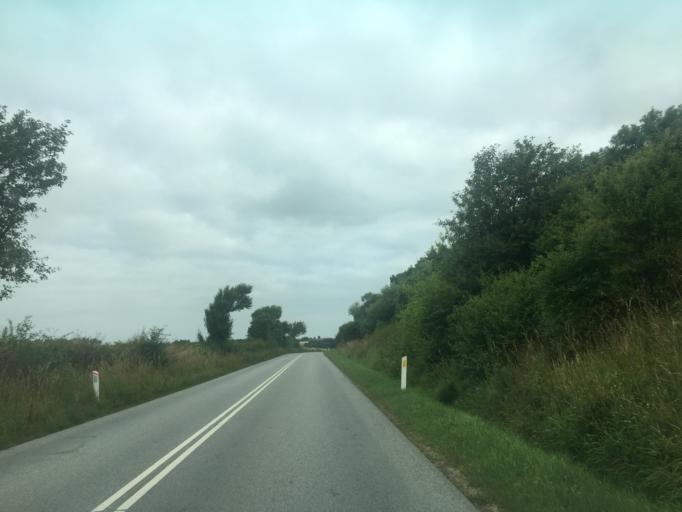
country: DK
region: North Denmark
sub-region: Thisted Kommune
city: Thisted
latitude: 56.8672
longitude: 8.6196
